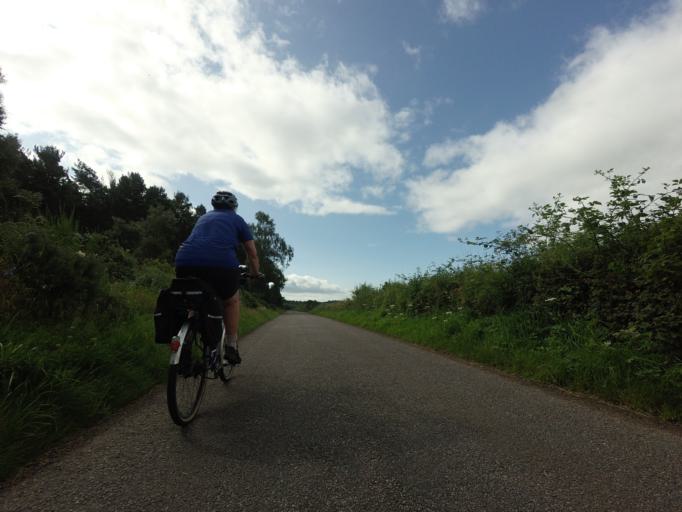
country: GB
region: Scotland
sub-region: Highland
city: Nairn
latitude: 57.5660
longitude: -3.8667
